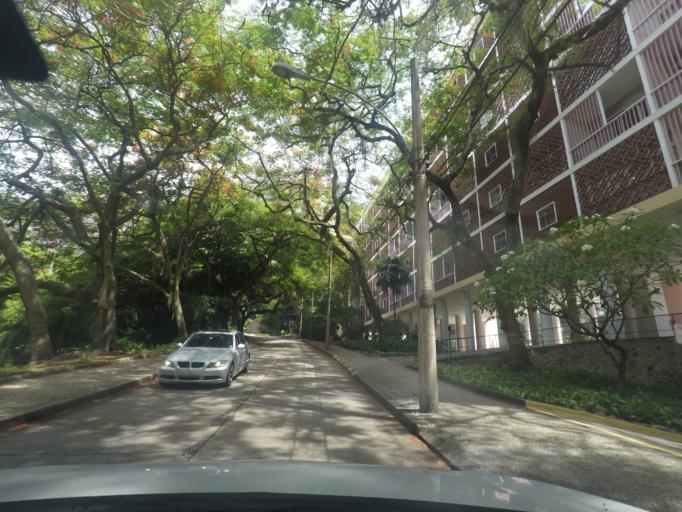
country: BR
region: Rio de Janeiro
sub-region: Rio De Janeiro
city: Rio de Janeiro
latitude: -22.9310
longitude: -43.1827
